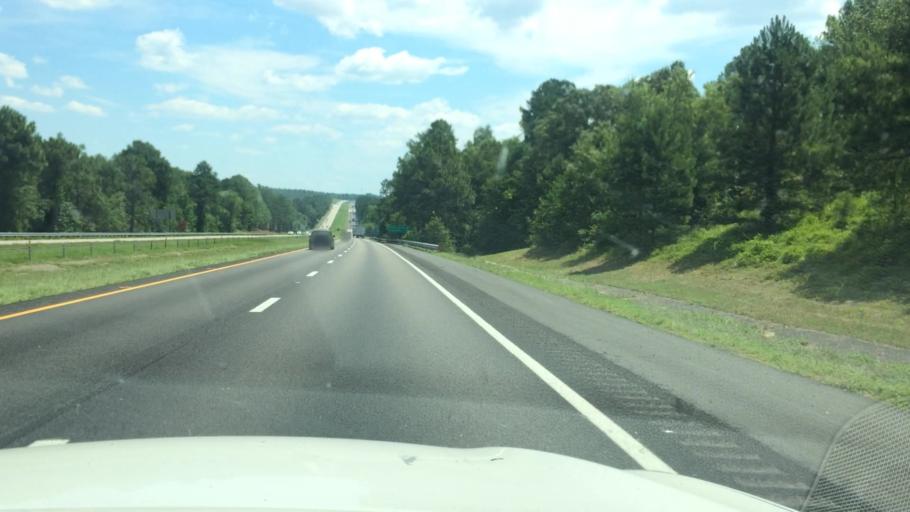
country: US
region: South Carolina
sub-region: Aiken County
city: Aiken
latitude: 33.6440
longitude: -81.7269
